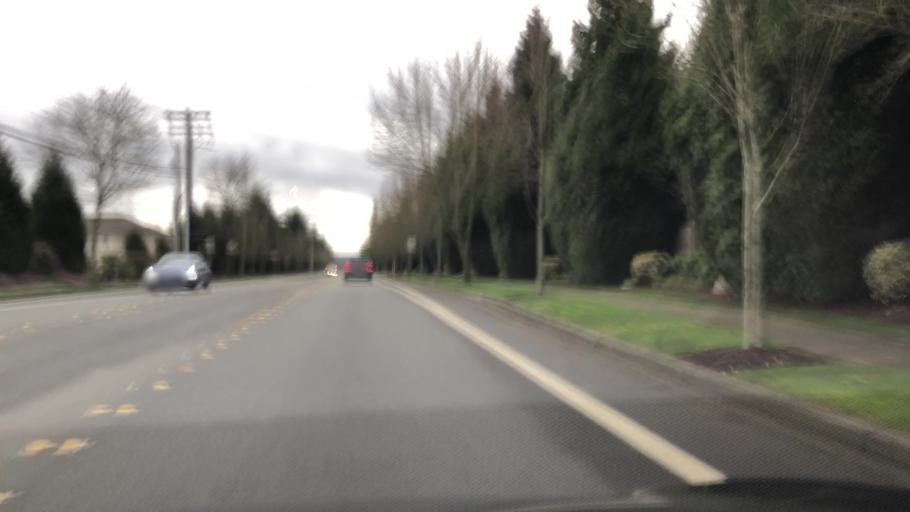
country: US
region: Washington
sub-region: Snohomish County
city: North Creek
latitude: 47.8107
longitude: -122.1808
